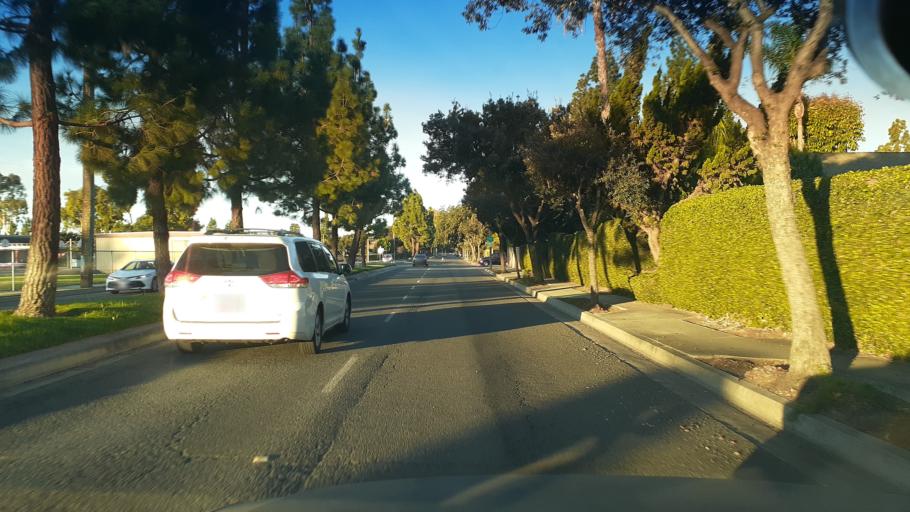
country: US
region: California
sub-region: Los Angeles County
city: Cerritos
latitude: 33.8534
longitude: -118.0745
